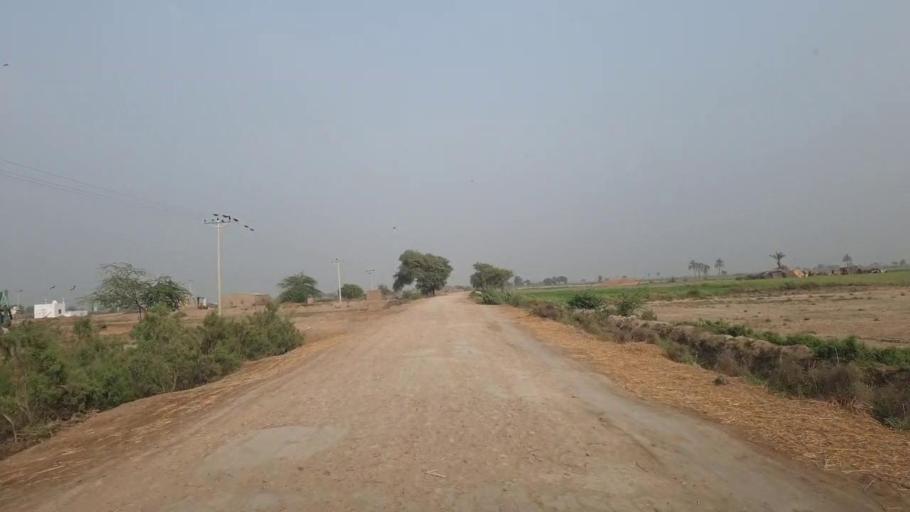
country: PK
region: Sindh
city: Mirpur Batoro
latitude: 24.5675
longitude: 68.4150
